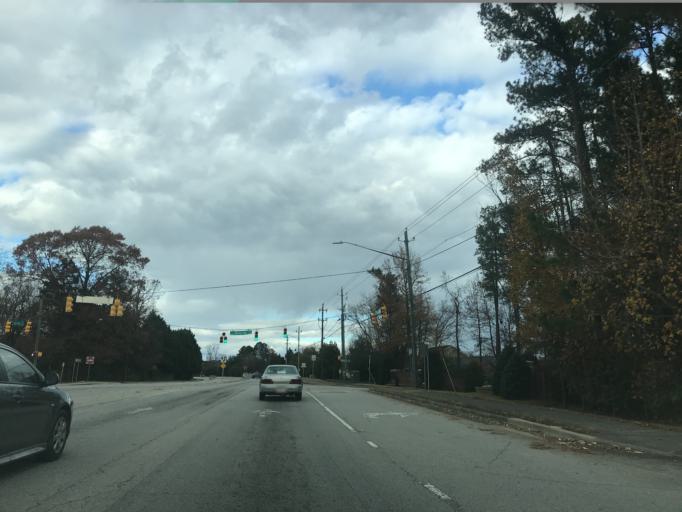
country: US
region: North Carolina
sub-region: Wake County
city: Raleigh
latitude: 35.8057
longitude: -78.5646
